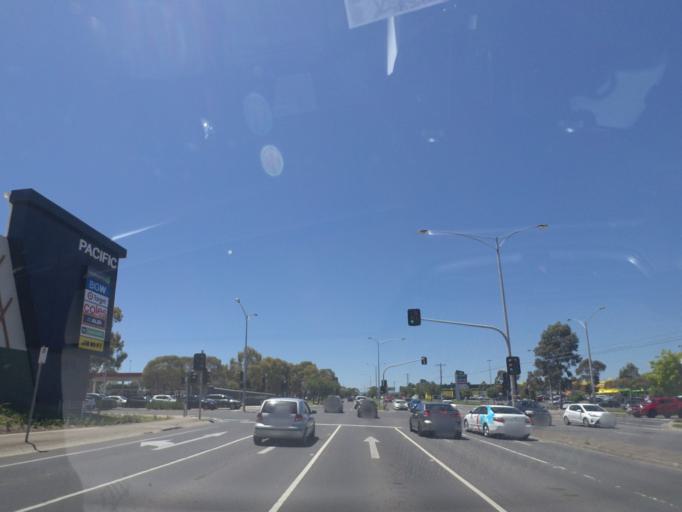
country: AU
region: Victoria
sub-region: Whittlesea
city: Lalor
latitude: -37.6555
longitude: 145.0212
